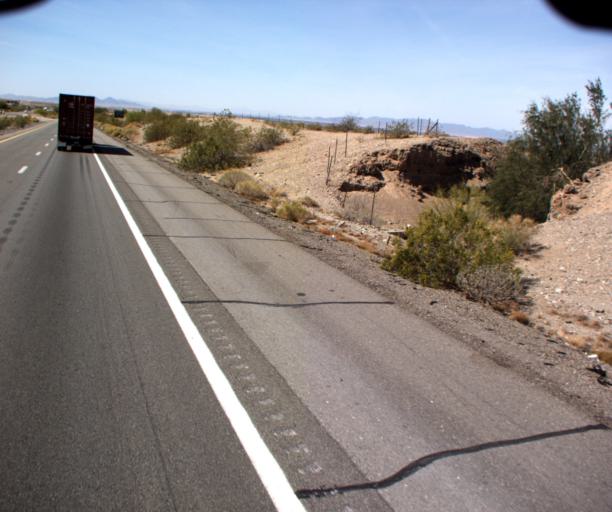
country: US
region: Arizona
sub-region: La Paz County
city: Ehrenberg
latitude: 33.6180
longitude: -114.4565
